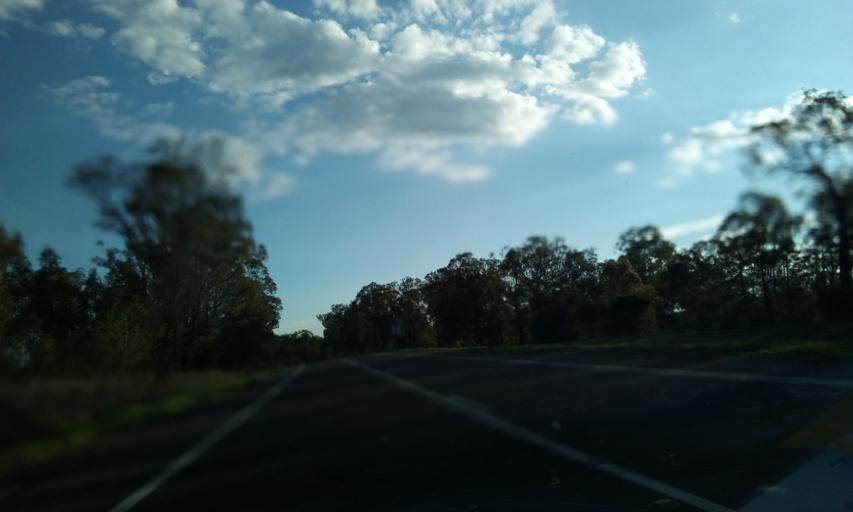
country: AU
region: New South Wales
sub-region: Camden
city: Camden South
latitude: -34.1096
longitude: 150.6972
